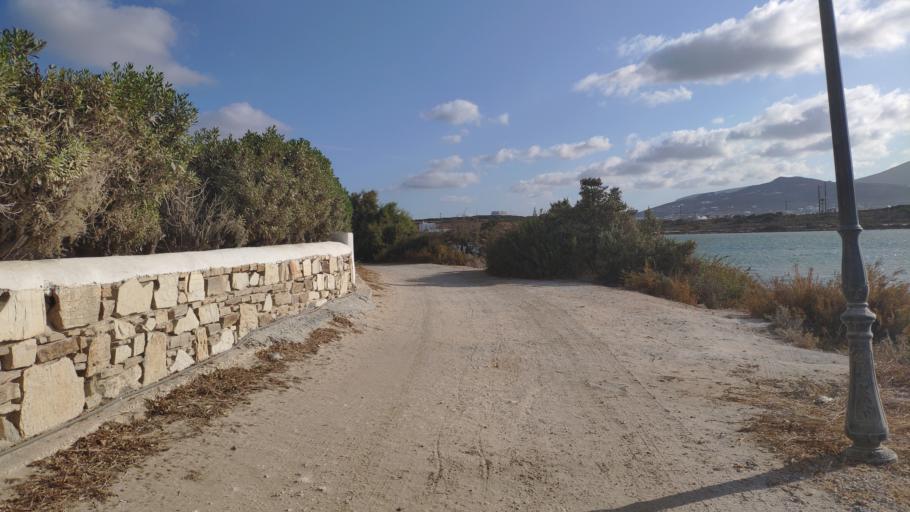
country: GR
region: South Aegean
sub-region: Nomos Kykladon
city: Antiparos
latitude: 37.0425
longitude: 25.0851
